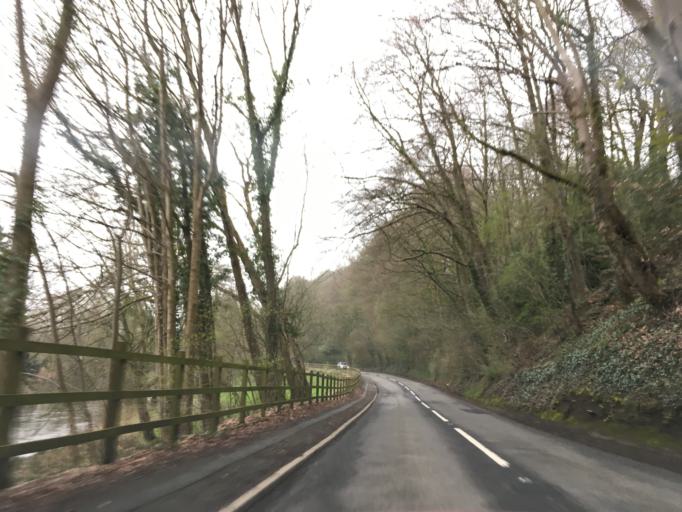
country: GB
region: Wales
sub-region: Monmouthshire
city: Usk
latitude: 51.7095
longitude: -2.9080
